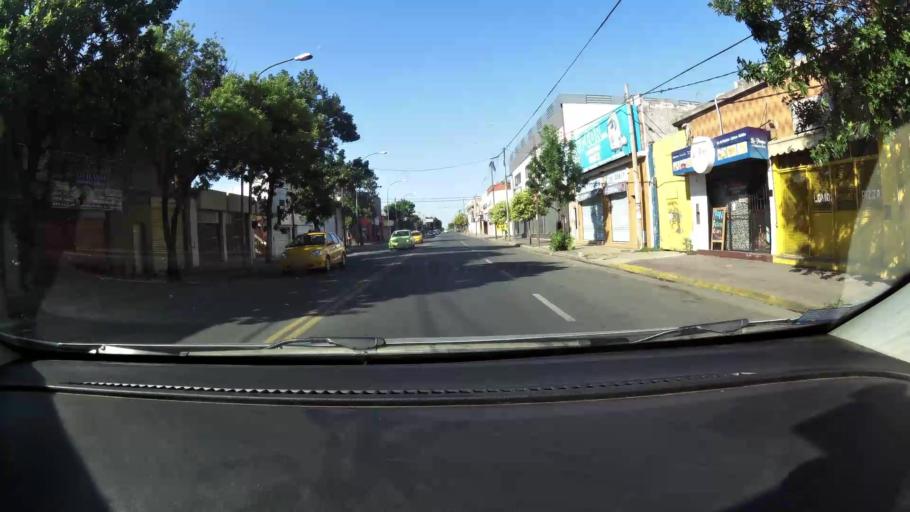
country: AR
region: Cordoba
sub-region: Departamento de Capital
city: Cordoba
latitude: -31.3919
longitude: -64.1648
